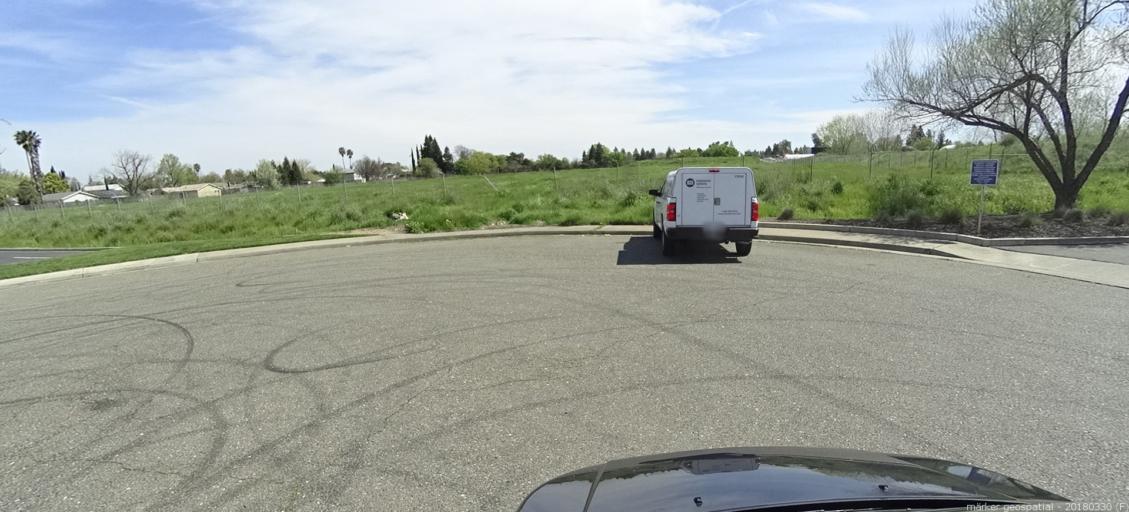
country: US
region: California
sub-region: Sacramento County
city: Rosemont
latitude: 38.5389
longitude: -121.3538
